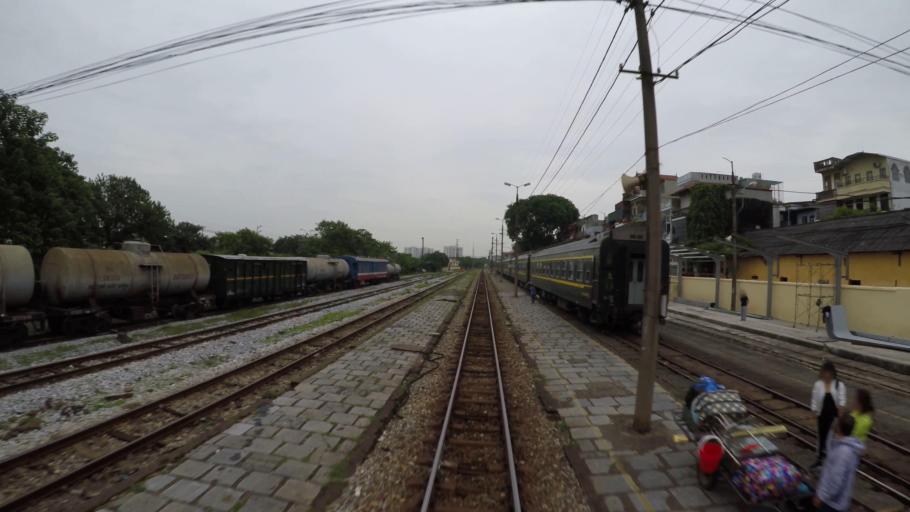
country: VN
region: Ha Noi
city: Trau Quy
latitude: 21.0322
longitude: 105.9087
